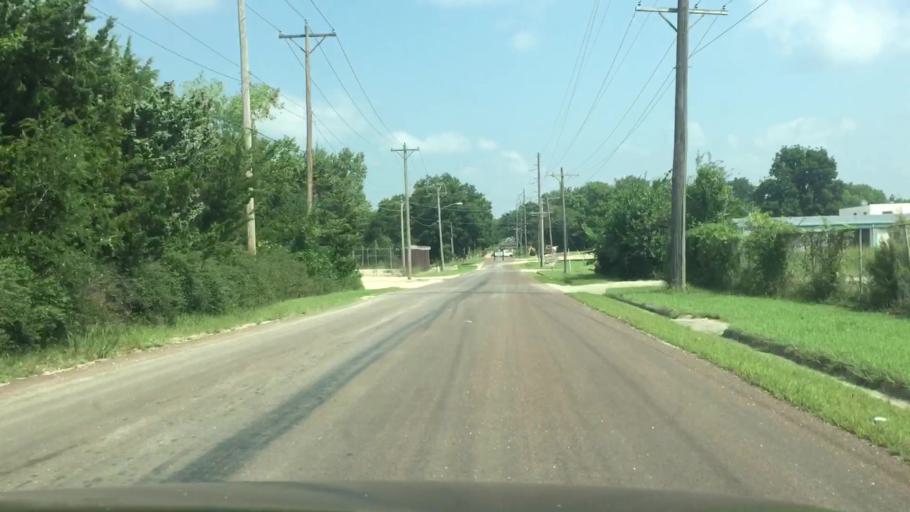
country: US
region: Kansas
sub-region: Allen County
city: Iola
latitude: 37.9080
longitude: -95.4056
